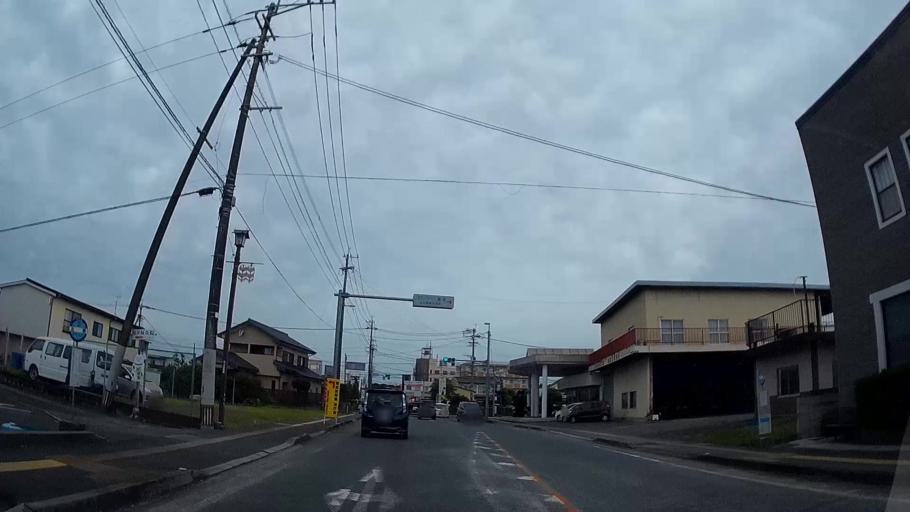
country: JP
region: Kumamoto
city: Kikuchi
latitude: 32.9780
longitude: 130.8068
